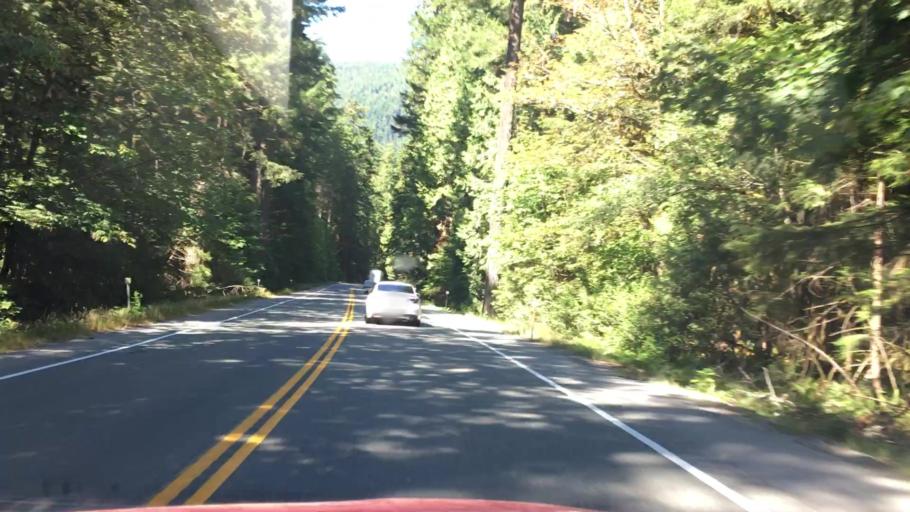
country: CA
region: British Columbia
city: Port Alberni
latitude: 49.2742
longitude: -124.6748
